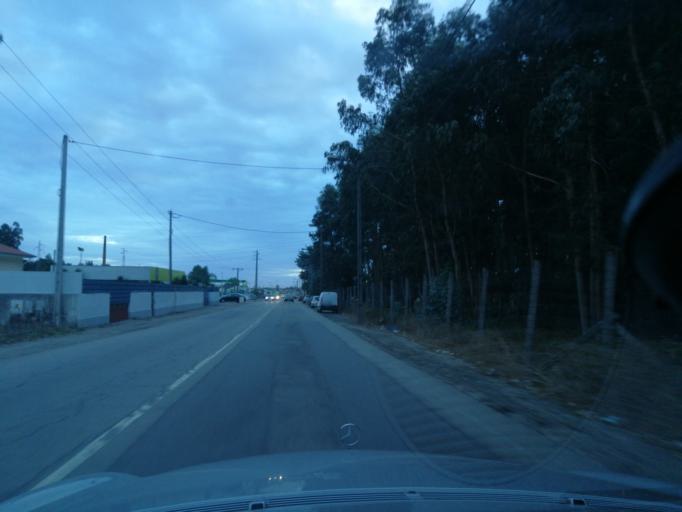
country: PT
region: Aveiro
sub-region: Estarreja
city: Beduido
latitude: 40.7731
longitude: -8.5691
